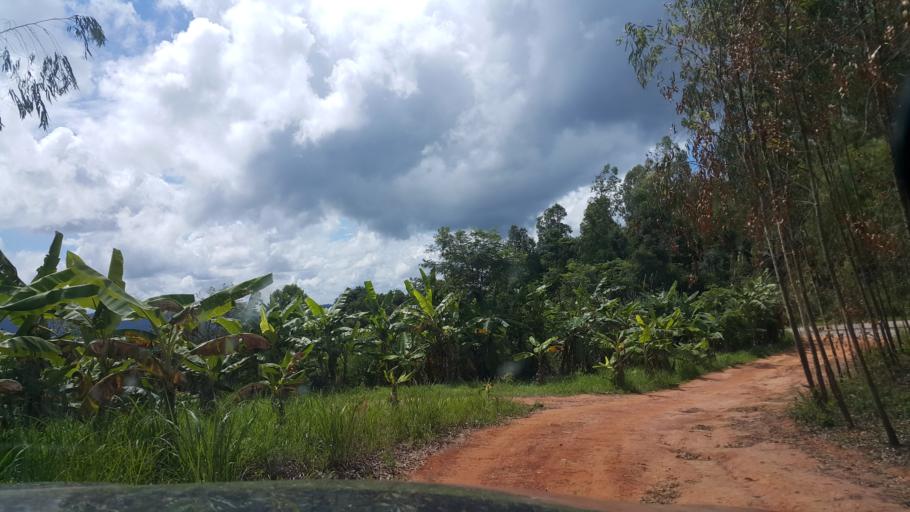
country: TH
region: Loei
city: Na Haeo
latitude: 17.5994
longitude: 100.8996
